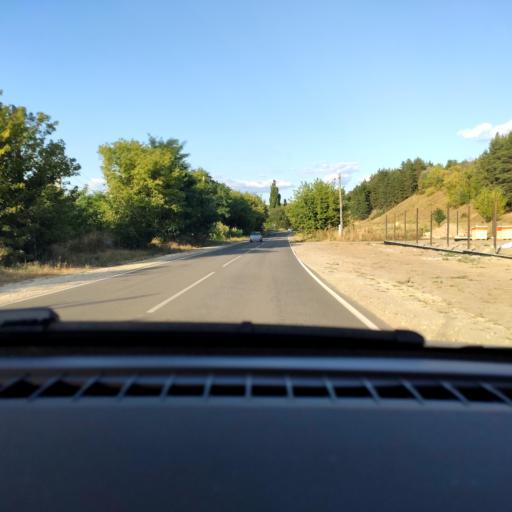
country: RU
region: Voronezj
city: Semiluki
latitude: 51.6664
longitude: 39.0167
